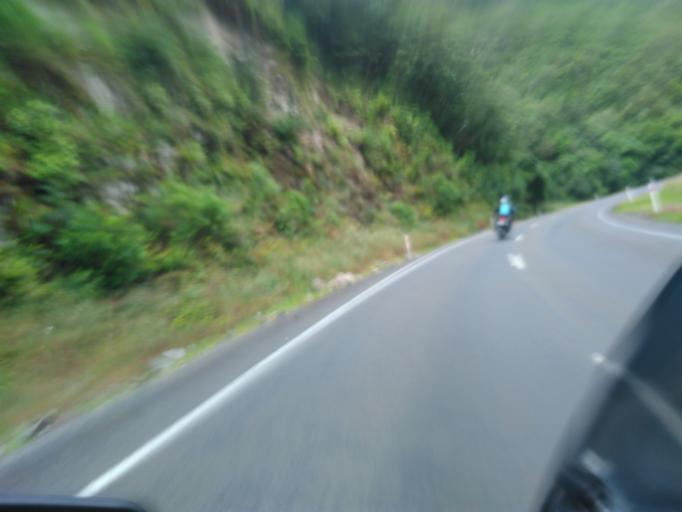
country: NZ
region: Bay of Plenty
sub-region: Opotiki District
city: Opotiki
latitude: -38.2977
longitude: 177.3917
